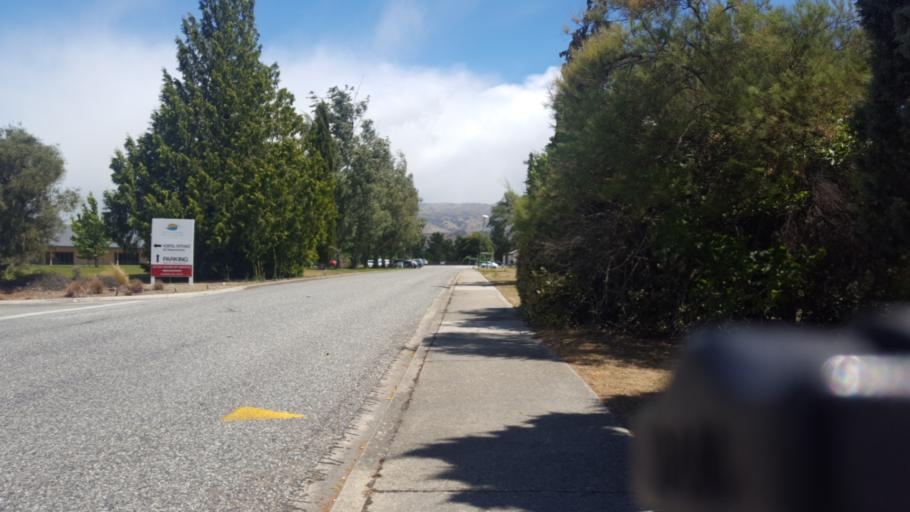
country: NZ
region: Otago
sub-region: Queenstown-Lakes District
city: Wanaka
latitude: -45.1998
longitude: 169.3309
